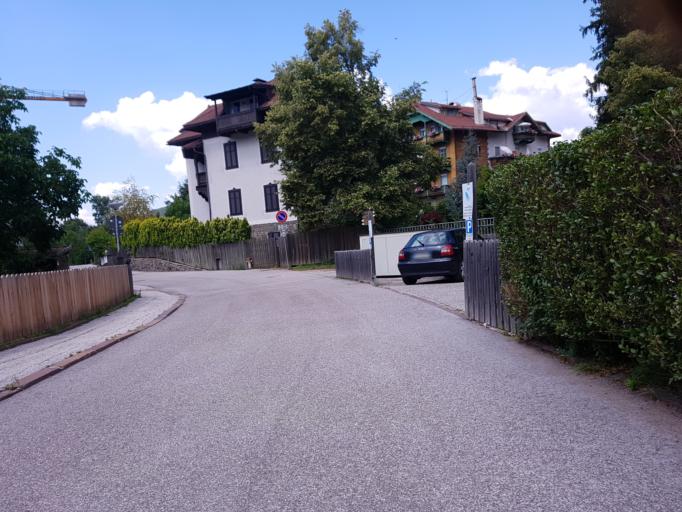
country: IT
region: Trentino-Alto Adige
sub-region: Bolzano
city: Siusi
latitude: 46.5439
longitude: 11.5655
